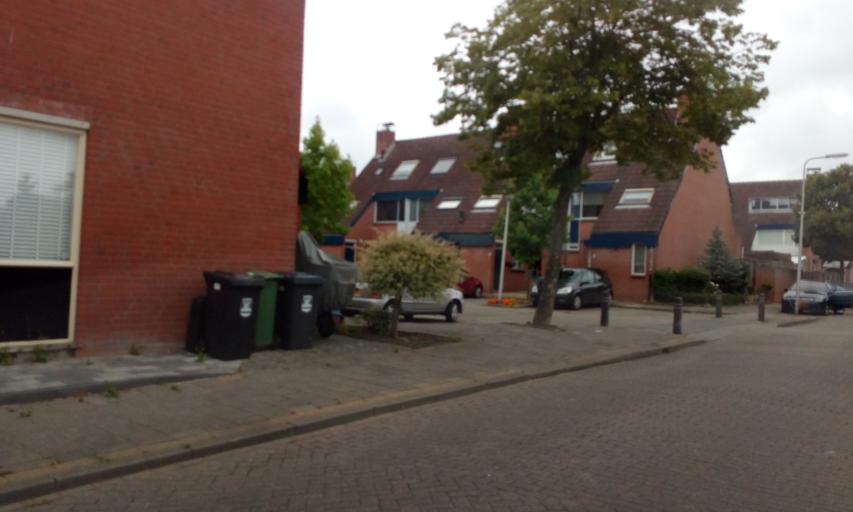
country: NL
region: South Holland
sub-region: Gemeente Westland
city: Kwintsheul
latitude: 52.0111
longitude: 4.2558
